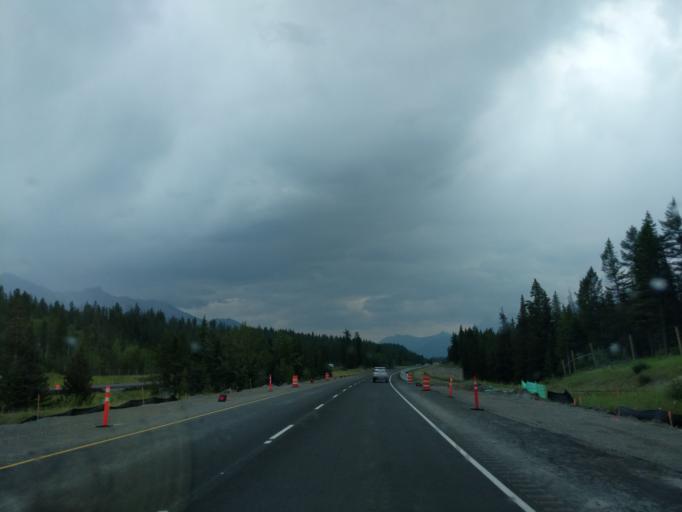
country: CA
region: Alberta
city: Canmore
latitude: 51.1621
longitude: -115.4424
